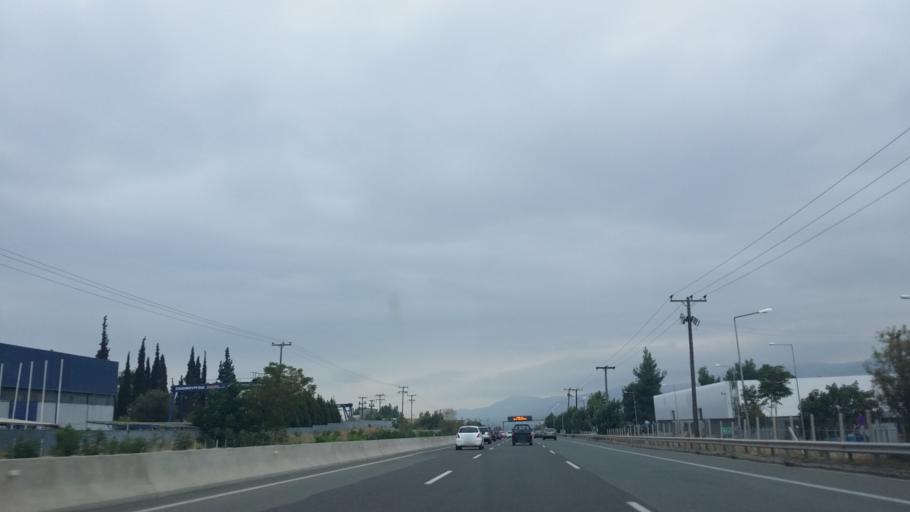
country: GR
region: Central Greece
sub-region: Nomos Voiotias
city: Oinofyta
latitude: 38.3183
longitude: 23.6255
